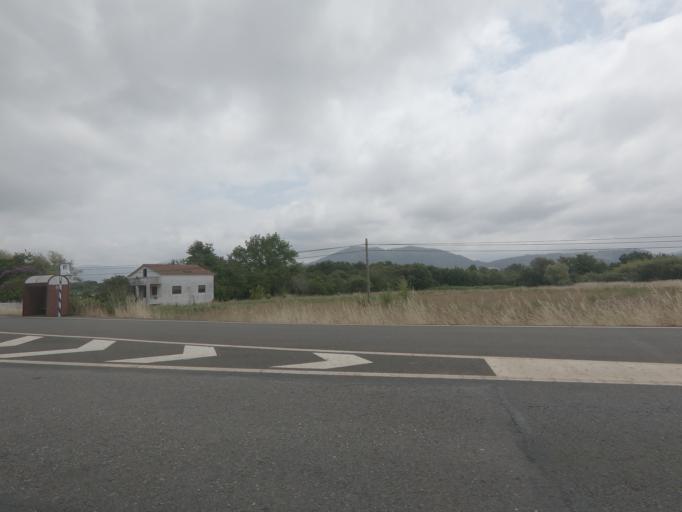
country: ES
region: Galicia
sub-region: Provincia de Pontevedra
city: O Rosal
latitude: 41.9212
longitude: -8.8114
